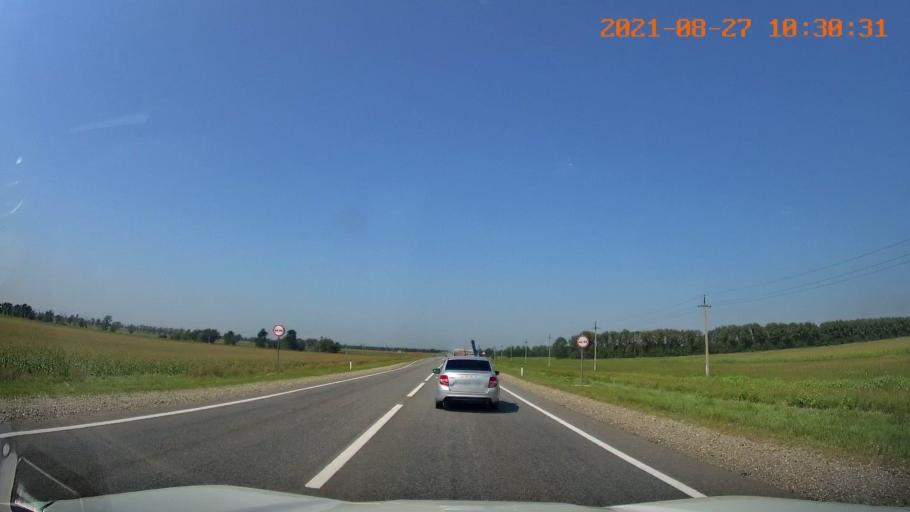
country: RU
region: Karachayevo-Cherkesiya
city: Kavkazskiy
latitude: 44.2628
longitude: 42.1764
